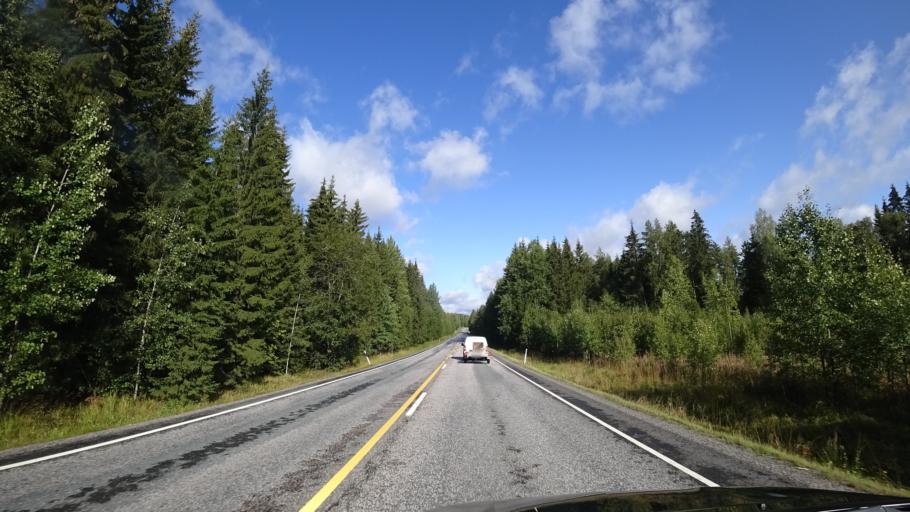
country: FI
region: Uusimaa
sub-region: Helsinki
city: Tuusula
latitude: 60.4537
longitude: 24.9550
